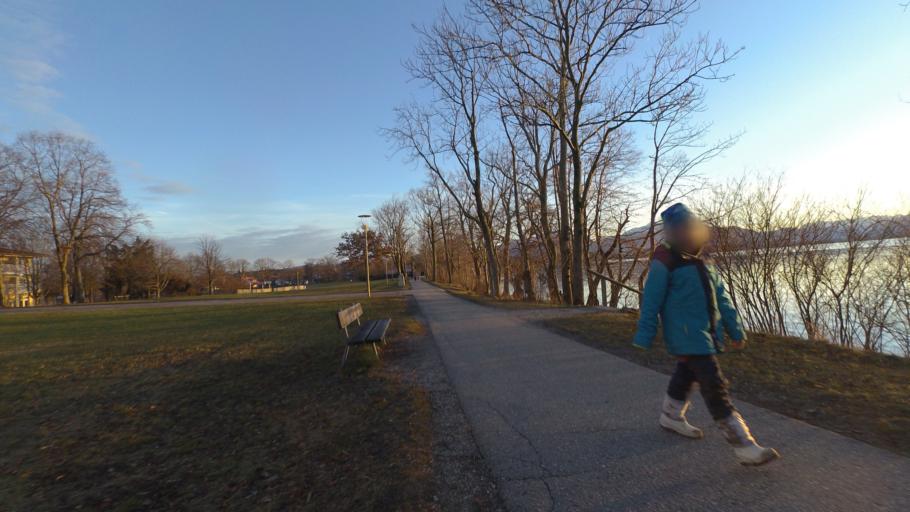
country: DE
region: Bavaria
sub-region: Upper Bavaria
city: Chieming
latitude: 47.8942
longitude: 12.5291
